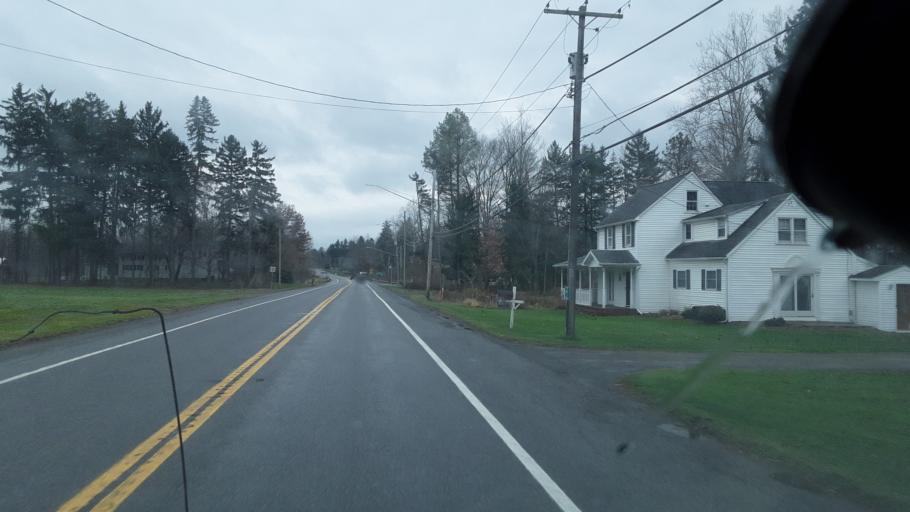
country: US
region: New York
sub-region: Erie County
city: Holland
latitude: 42.6777
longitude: -78.5623
